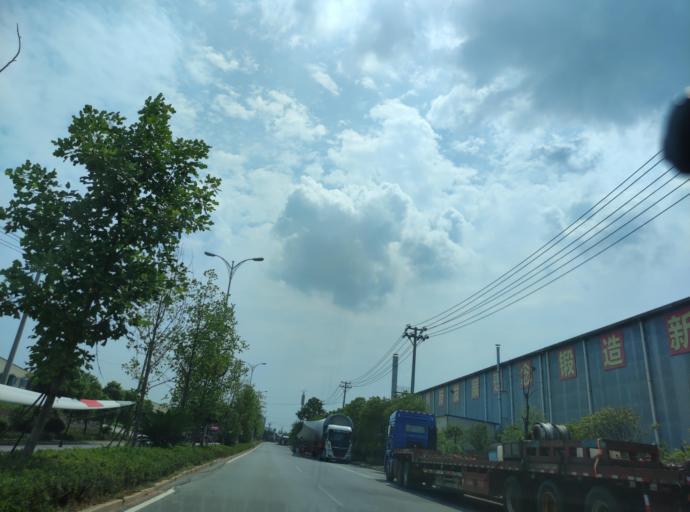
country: CN
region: Jiangxi Sheng
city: Yuannan
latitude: 27.6648
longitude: 114.0106
